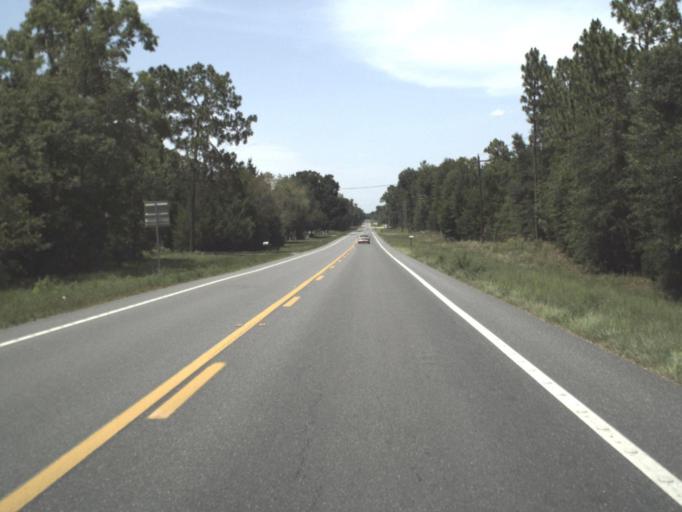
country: US
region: Florida
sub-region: Gilchrist County
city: Trenton
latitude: 29.8040
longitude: -82.8670
